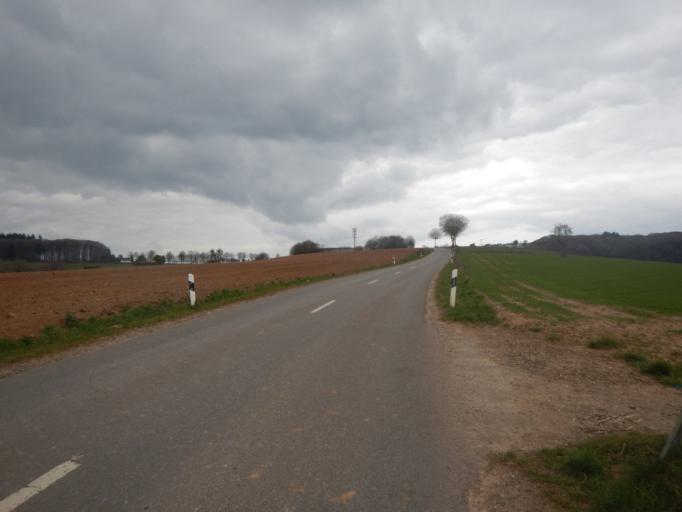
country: LU
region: Diekirch
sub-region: Canton de Redange
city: Ell
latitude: 49.7904
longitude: 5.8341
